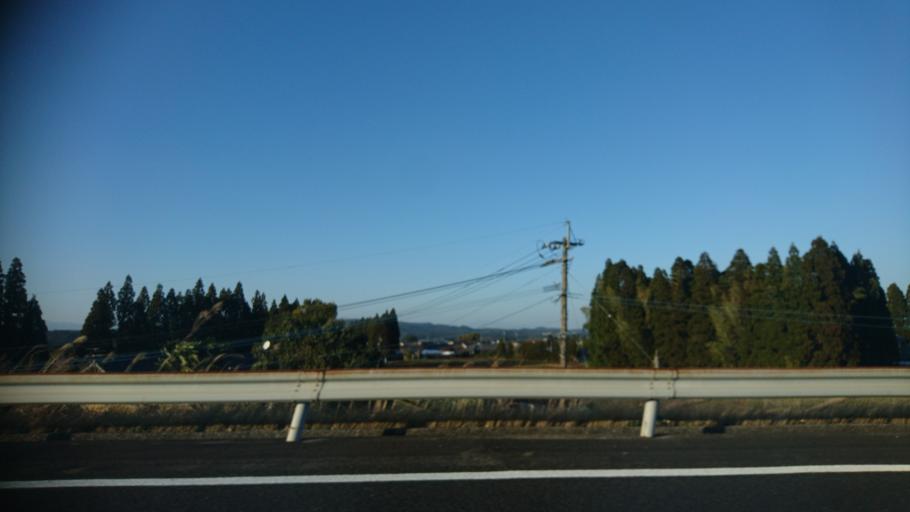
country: JP
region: Miyazaki
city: Miyazaki-shi
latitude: 31.8202
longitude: 131.2898
